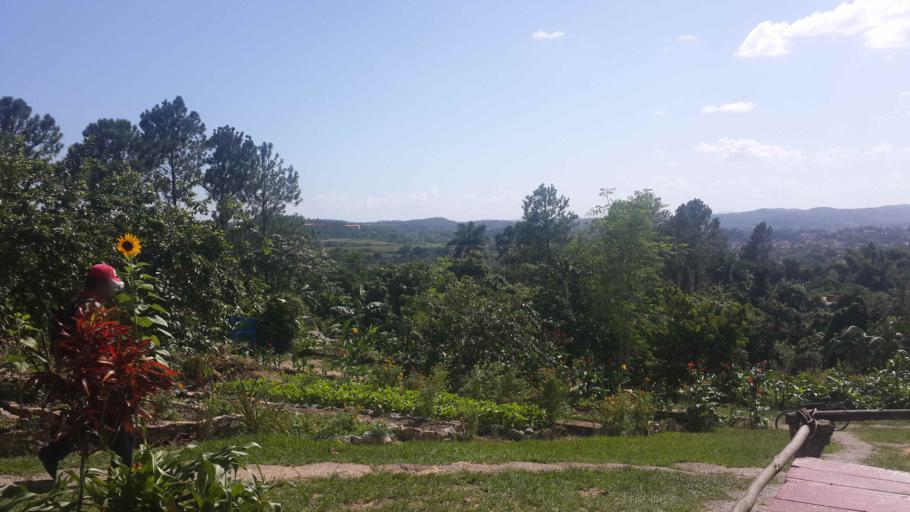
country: CU
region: Pinar del Rio
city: Vinales
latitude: 22.6250
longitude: -83.6916
